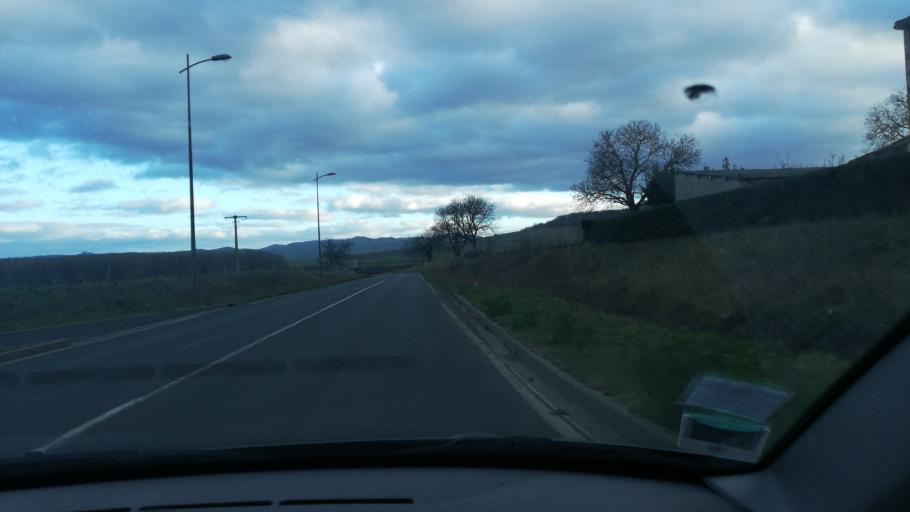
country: FR
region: Auvergne
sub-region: Departement du Puy-de-Dome
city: Vertaizon
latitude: 45.7624
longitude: 3.3074
